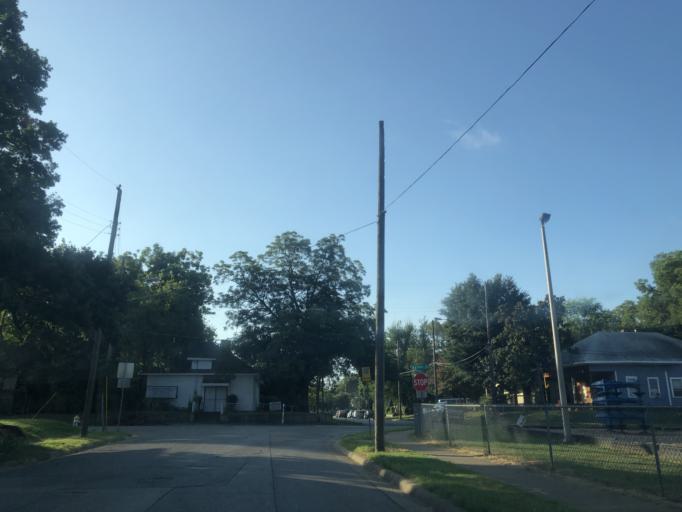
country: US
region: Texas
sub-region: Dallas County
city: Dallas
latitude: 32.7611
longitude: -96.7723
